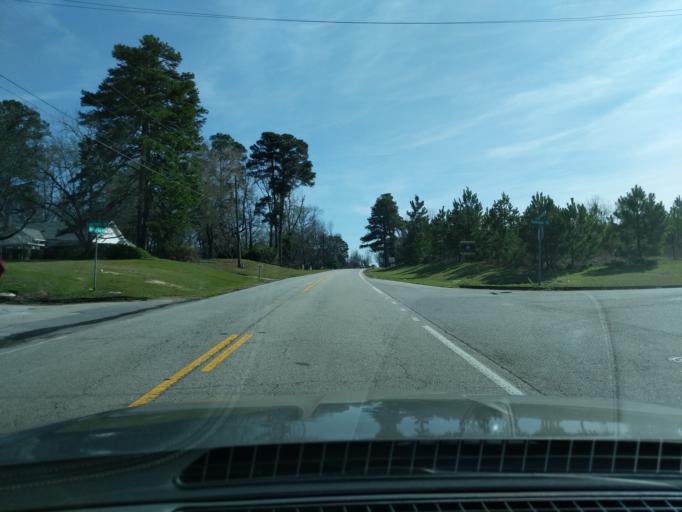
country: US
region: Georgia
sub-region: Columbia County
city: Evans
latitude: 33.5335
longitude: -82.1365
